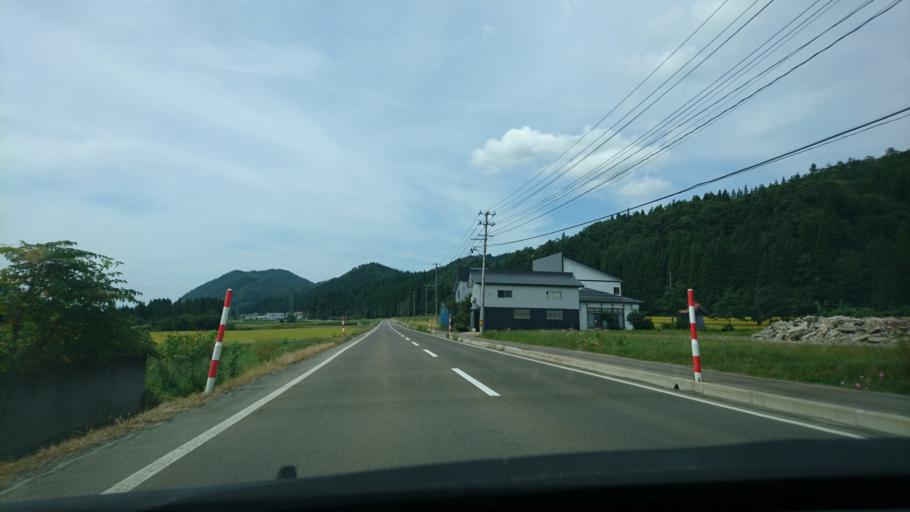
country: JP
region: Akita
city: Yuzawa
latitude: 39.1950
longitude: 140.6151
